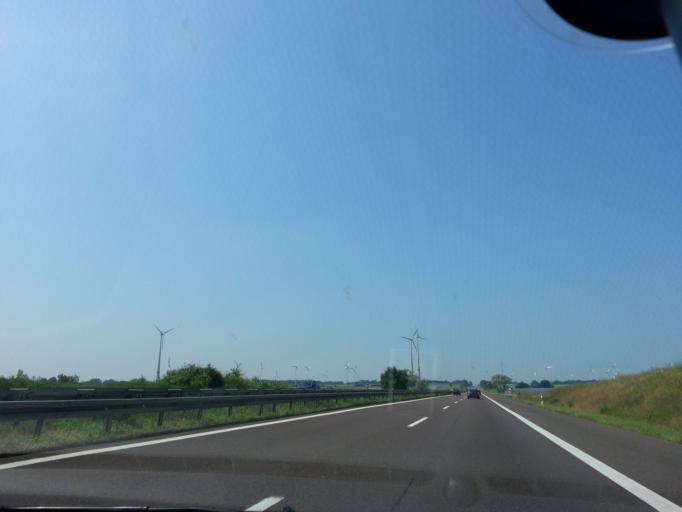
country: DE
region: Brandenburg
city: Gerdshagen
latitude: 53.2094
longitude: 12.2540
